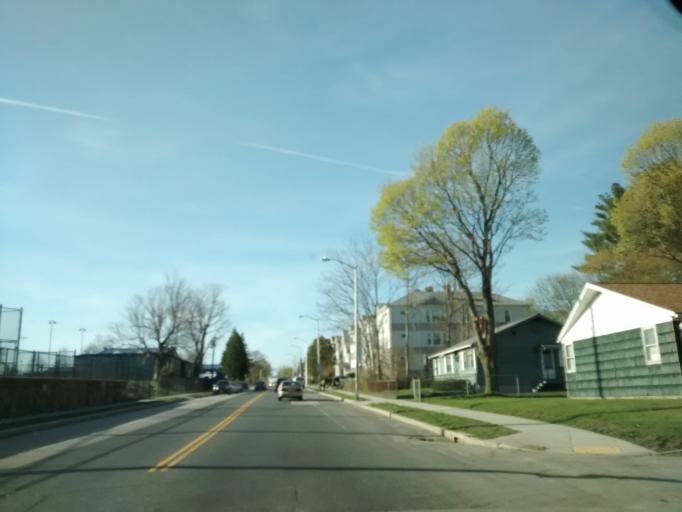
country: US
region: Massachusetts
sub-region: Worcester County
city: Sunderland
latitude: 42.2429
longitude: -71.7912
